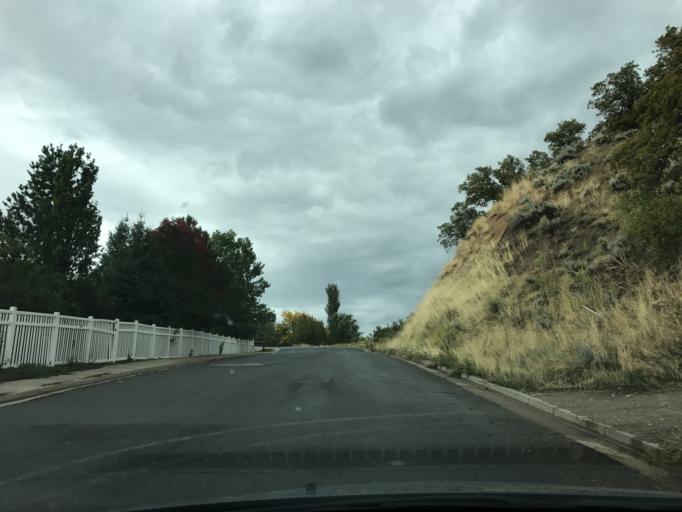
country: US
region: Utah
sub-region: Davis County
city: Fruit Heights
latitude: 41.0200
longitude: -111.8991
